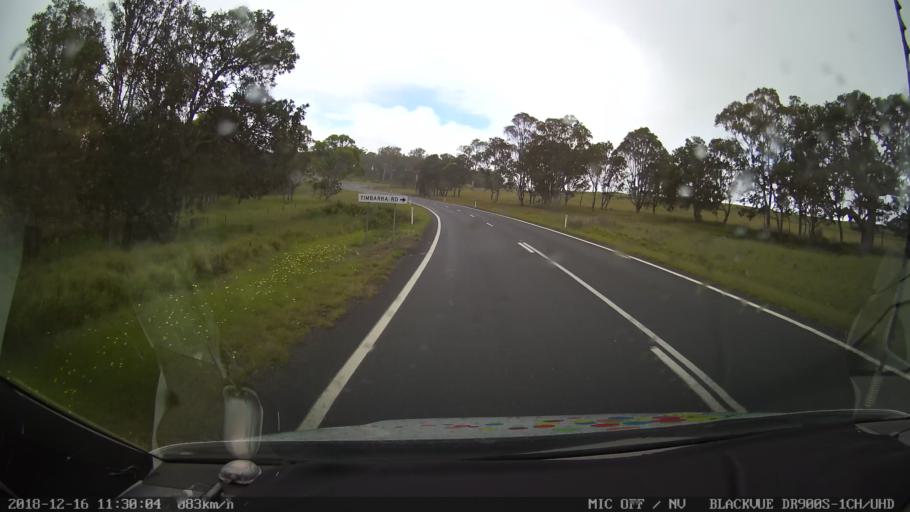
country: AU
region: New South Wales
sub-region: Tenterfield Municipality
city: Carrolls Creek
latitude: -29.0359
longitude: 152.1173
